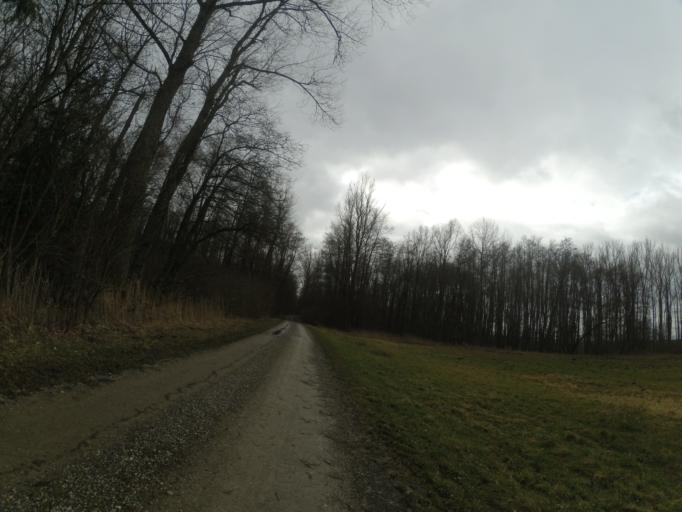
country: DE
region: Bavaria
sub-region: Swabia
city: Vohringen
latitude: 48.2972
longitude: 10.0933
